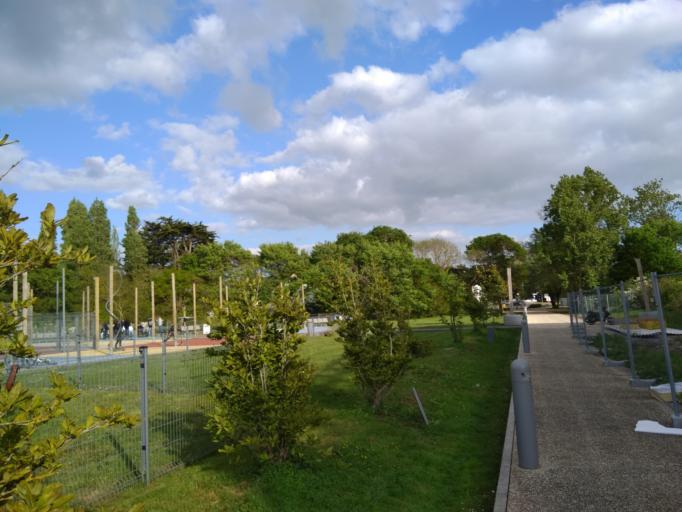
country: FR
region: Pays de la Loire
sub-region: Departement de la Loire-Atlantique
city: Pornichet
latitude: 47.2589
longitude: -2.3258
